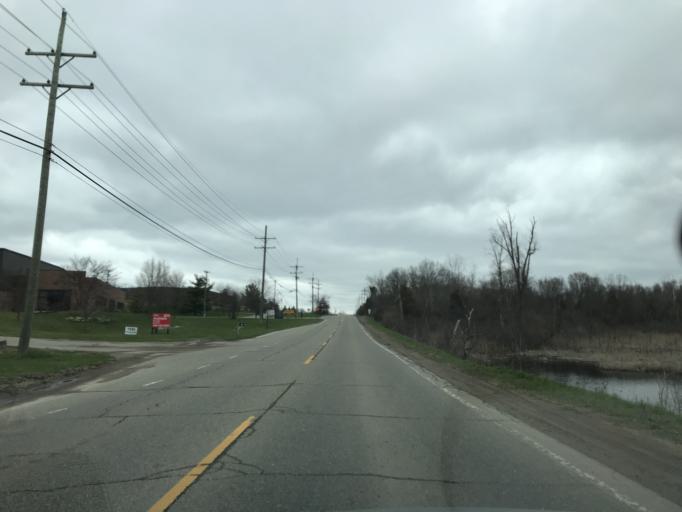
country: US
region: Michigan
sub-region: Oakland County
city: South Lyon
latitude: 42.4975
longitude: -83.6890
